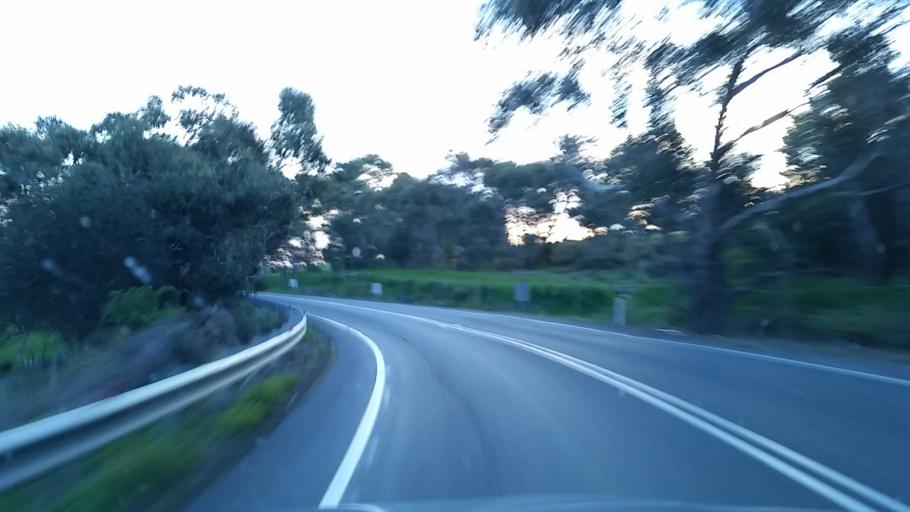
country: AU
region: South Australia
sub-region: Yankalilla
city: Normanville
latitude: -35.4163
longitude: 138.4248
